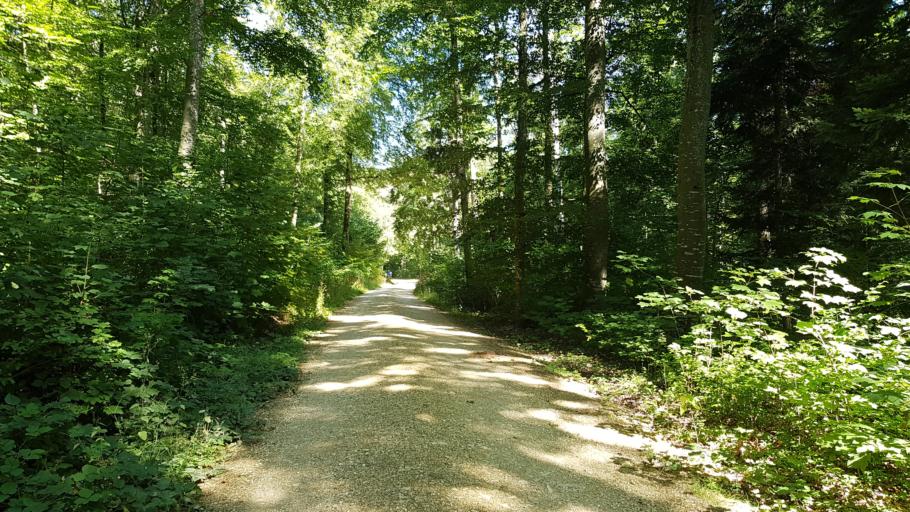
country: CH
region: Schaffhausen
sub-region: Bezirk Schaffhausen
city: Beringen
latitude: 47.7455
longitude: 8.5800
